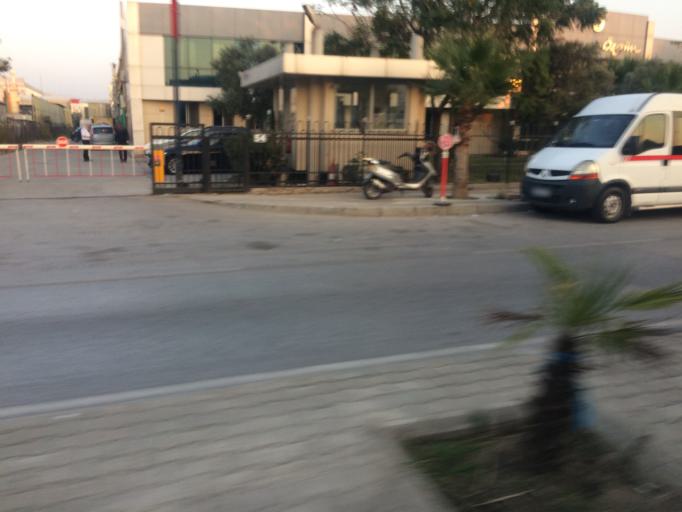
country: TR
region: Izmir
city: Karsiyaka
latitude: 38.4981
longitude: 27.0371
